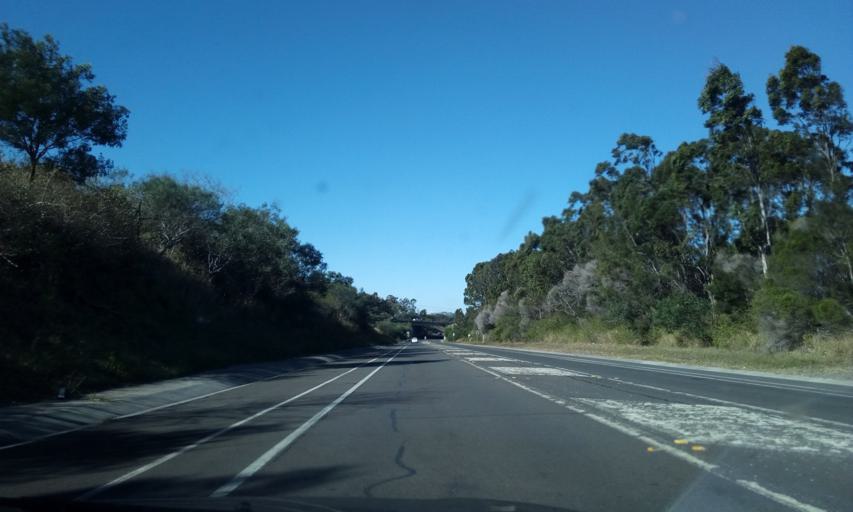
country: AU
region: New South Wales
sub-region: Wollongong
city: Dapto
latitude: -34.5208
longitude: 150.7857
